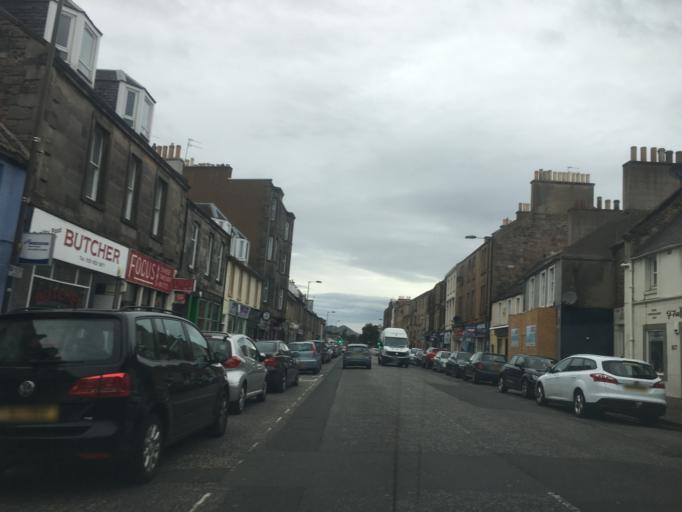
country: GB
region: Scotland
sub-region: East Lothian
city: Musselburgh
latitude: 55.9439
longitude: -3.0598
